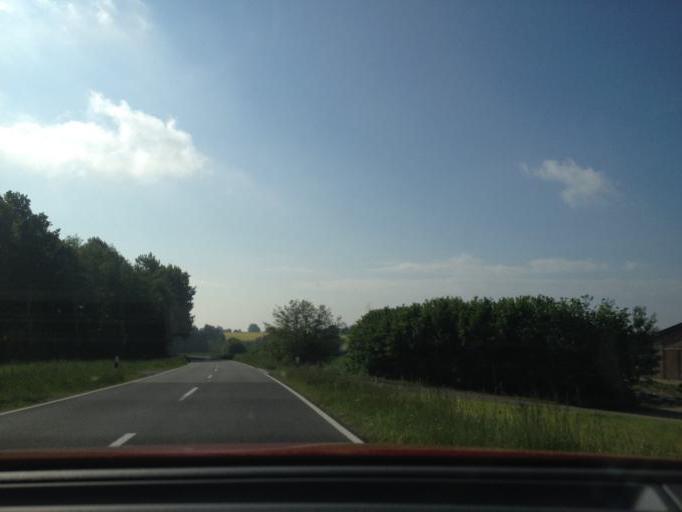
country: DE
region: Bavaria
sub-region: Upper Palatinate
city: Kirchenthumbach
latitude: 49.7659
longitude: 11.6787
